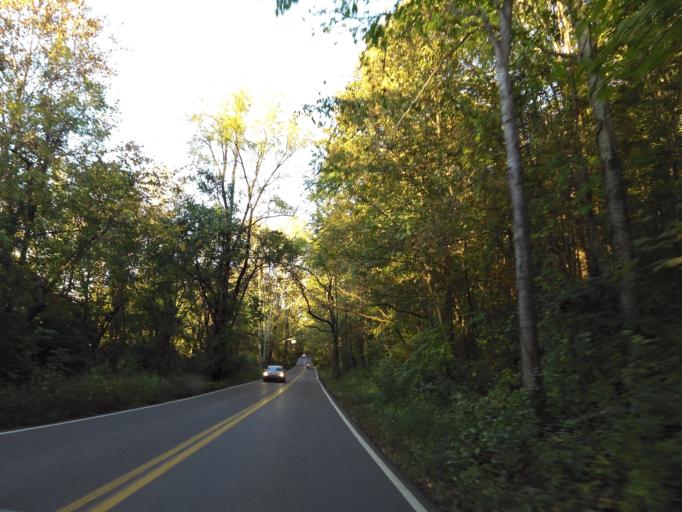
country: US
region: Tennessee
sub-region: Knox County
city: Knoxville
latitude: 36.0408
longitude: -83.9560
